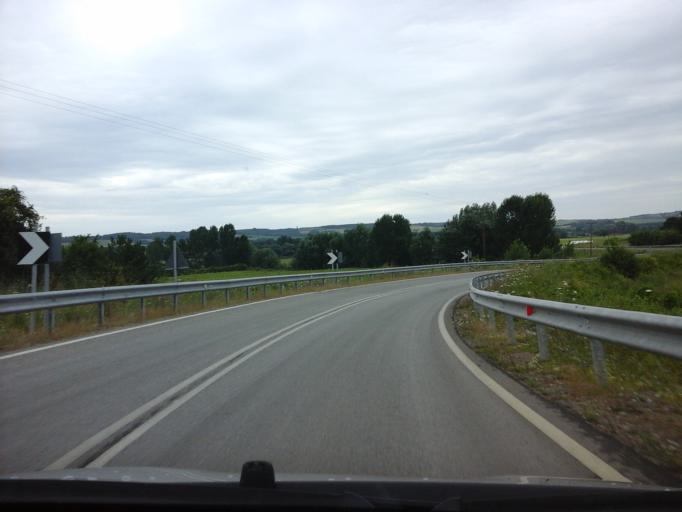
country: GR
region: East Macedonia and Thrace
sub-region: Nomos Evrou
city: Soufli
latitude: 41.1342
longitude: 26.2402
